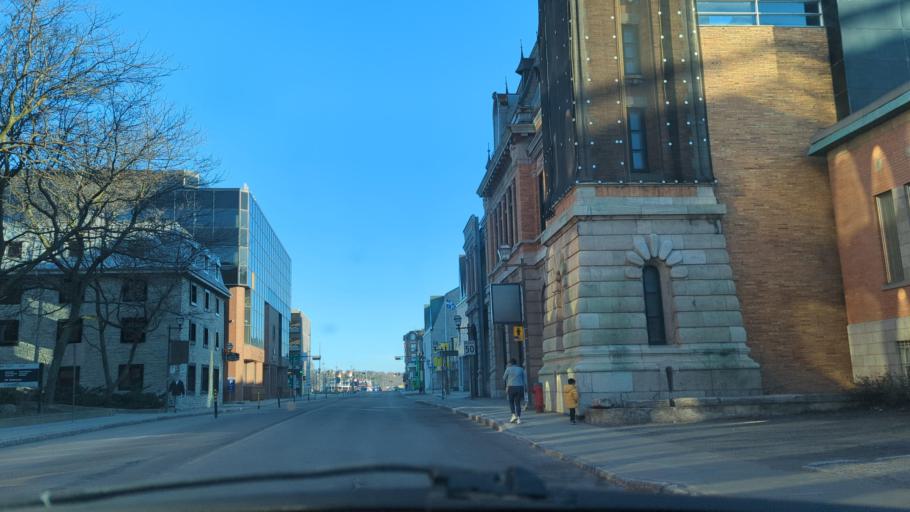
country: CA
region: Quebec
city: Quebec
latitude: 46.8164
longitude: -71.2023
